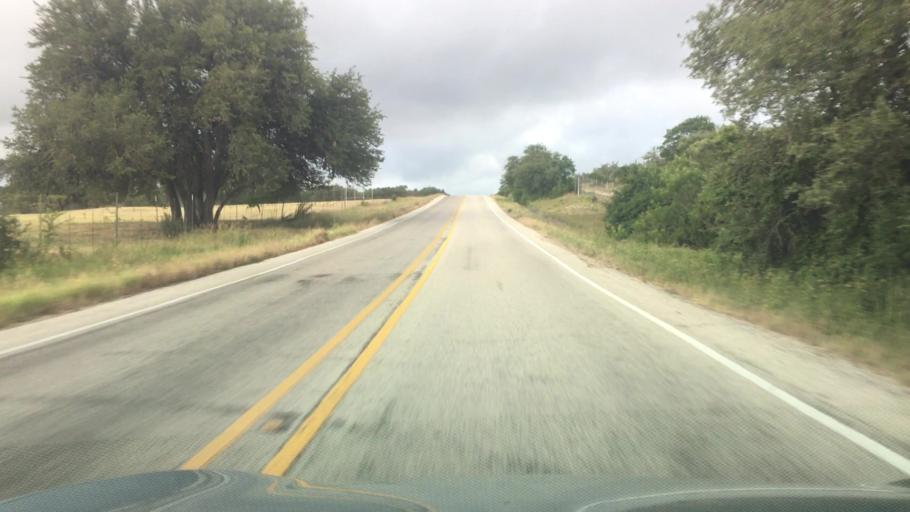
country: US
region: Texas
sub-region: Hays County
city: Dripping Springs
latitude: 30.1533
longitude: -98.2535
